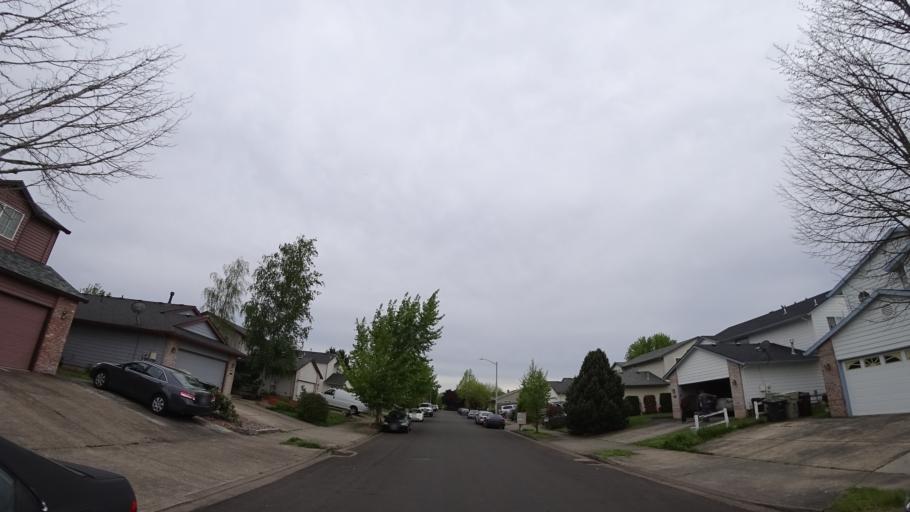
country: US
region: Oregon
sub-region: Washington County
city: Aloha
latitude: 45.5151
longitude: -122.9052
